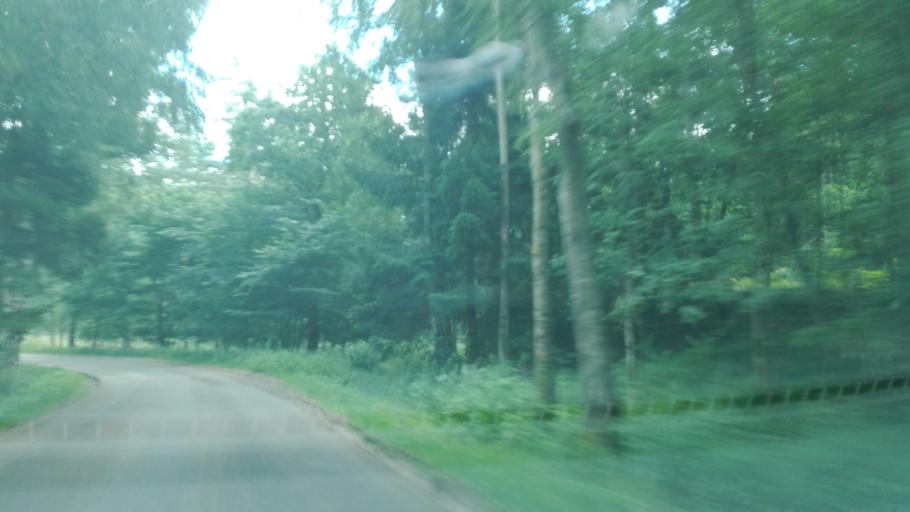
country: DK
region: Central Jutland
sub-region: Silkeborg Kommune
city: Svejbaek
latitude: 56.0818
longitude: 9.6041
